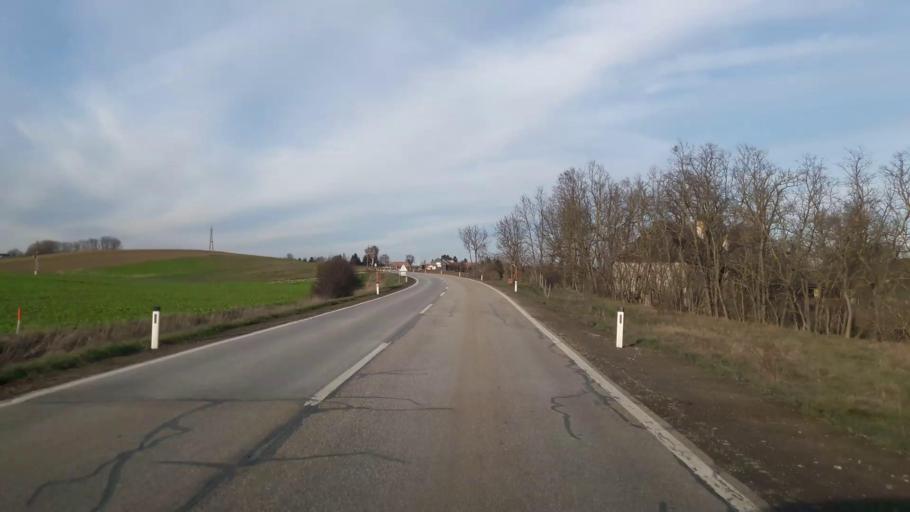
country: AT
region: Lower Austria
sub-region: Politischer Bezirk Ganserndorf
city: Bad Pirawarth
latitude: 48.4393
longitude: 16.6059
